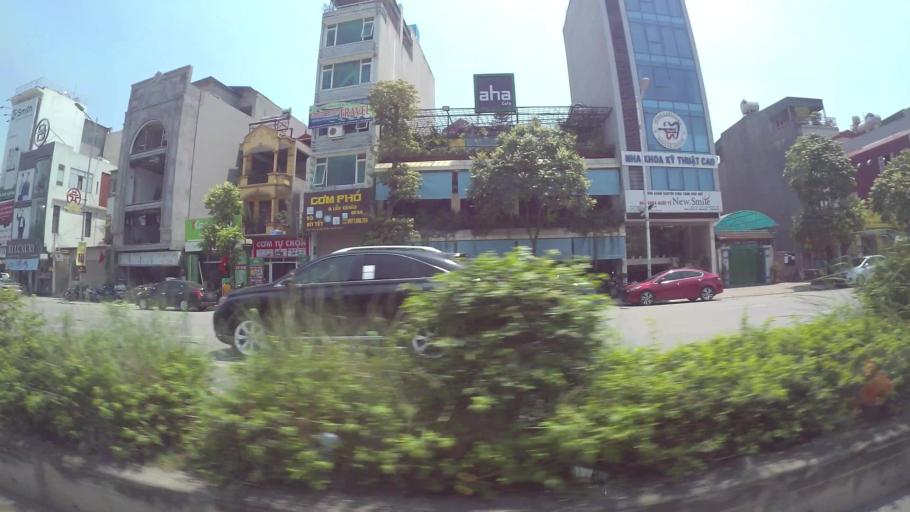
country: VN
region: Ha Noi
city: Hoan Kiem
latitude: 21.0436
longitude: 105.8729
